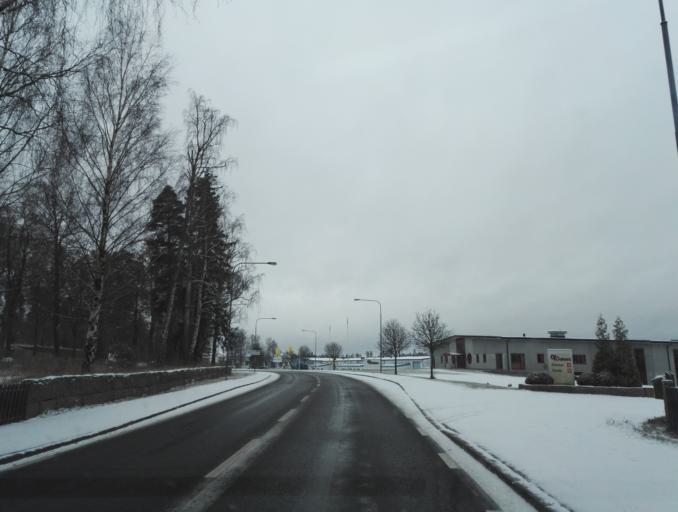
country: SE
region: Kronoberg
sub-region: Lessebo Kommun
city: Lessebo
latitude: 56.7464
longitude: 15.2691
